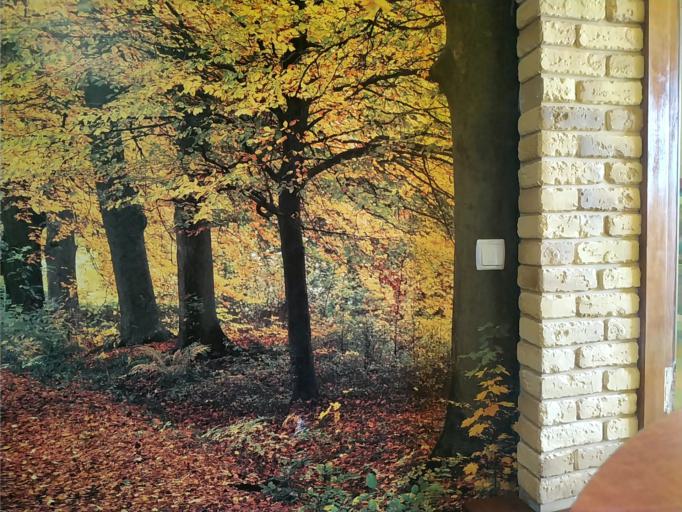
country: RU
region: Vologda
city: Nelazskoye
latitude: 59.4571
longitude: 37.6063
